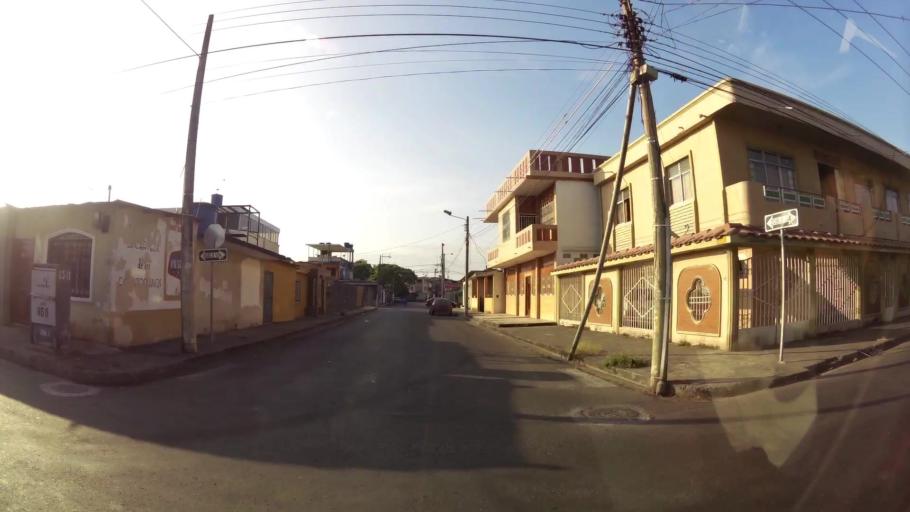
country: EC
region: Guayas
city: Eloy Alfaro
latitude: -2.1776
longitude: -79.8566
